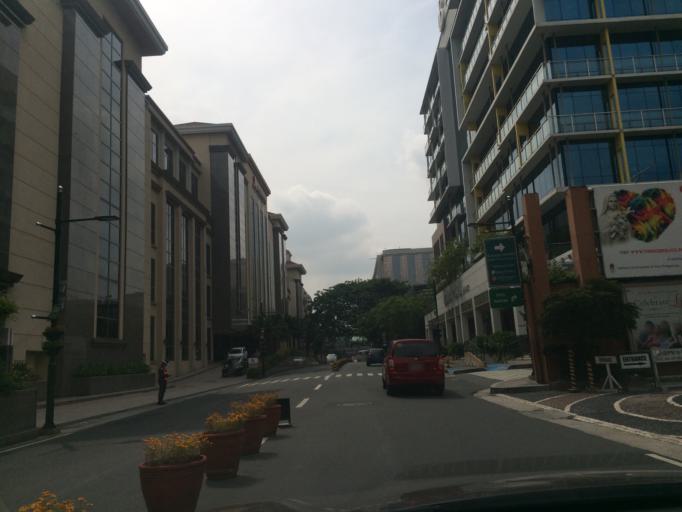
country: PH
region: Metro Manila
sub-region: Makati City
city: Makati City
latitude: 14.5217
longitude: 121.0164
